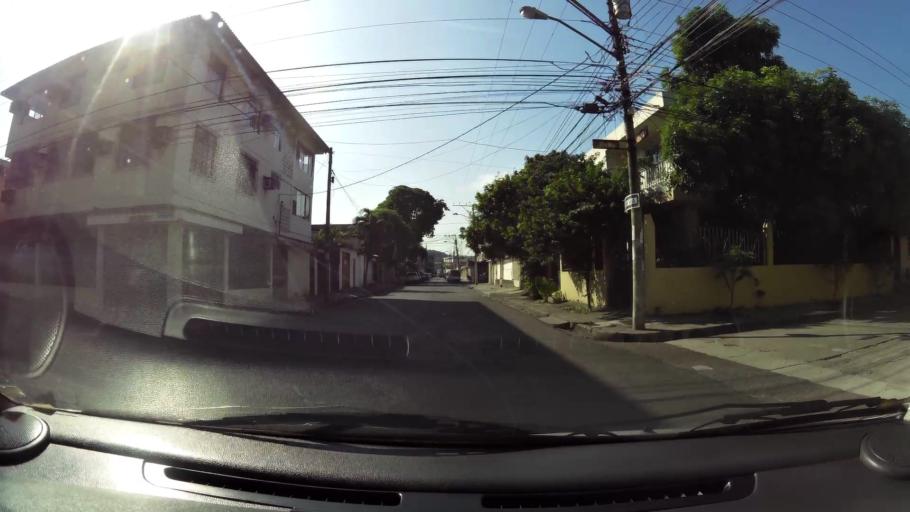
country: EC
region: Guayas
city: Guayaquil
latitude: -2.1773
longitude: -79.8993
